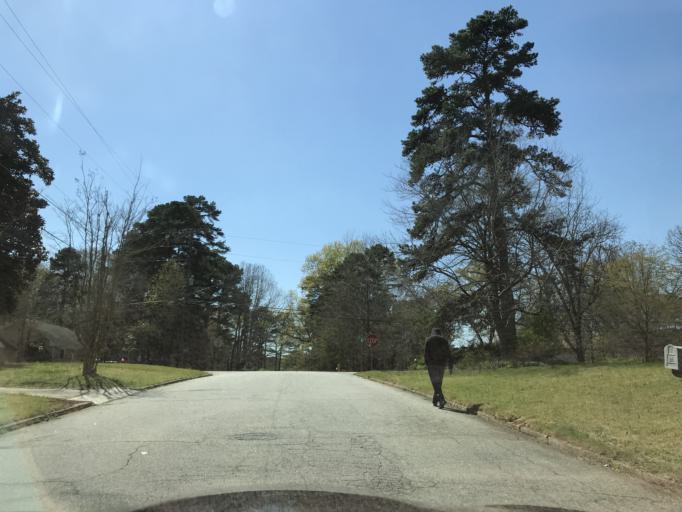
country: US
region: North Carolina
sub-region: Wake County
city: West Raleigh
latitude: 35.7689
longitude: -78.6974
